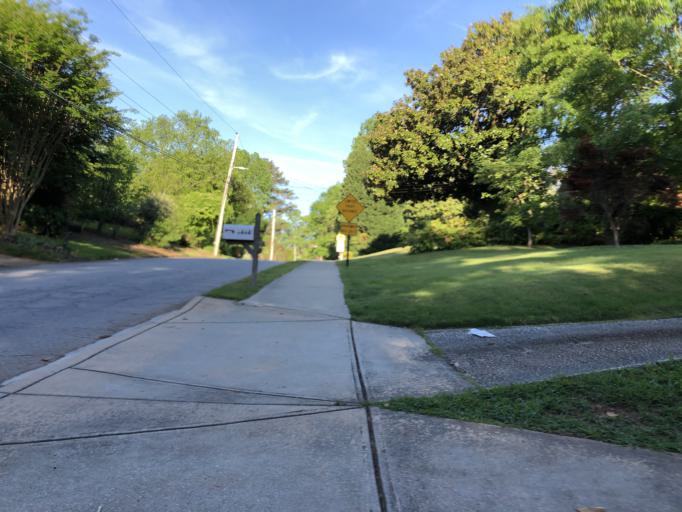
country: US
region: Georgia
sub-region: DeKalb County
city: North Decatur
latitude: 33.7806
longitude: -84.3152
